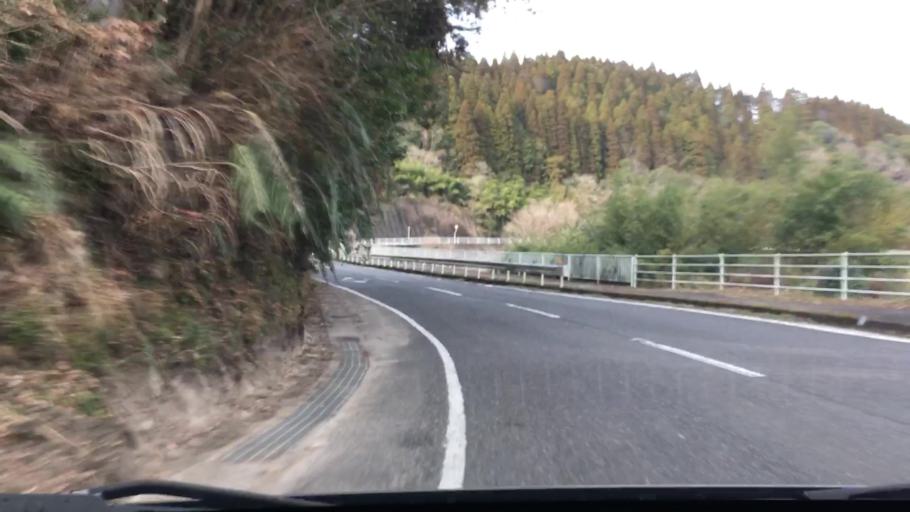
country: JP
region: Miyazaki
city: Kushima
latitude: 31.5455
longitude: 131.2423
